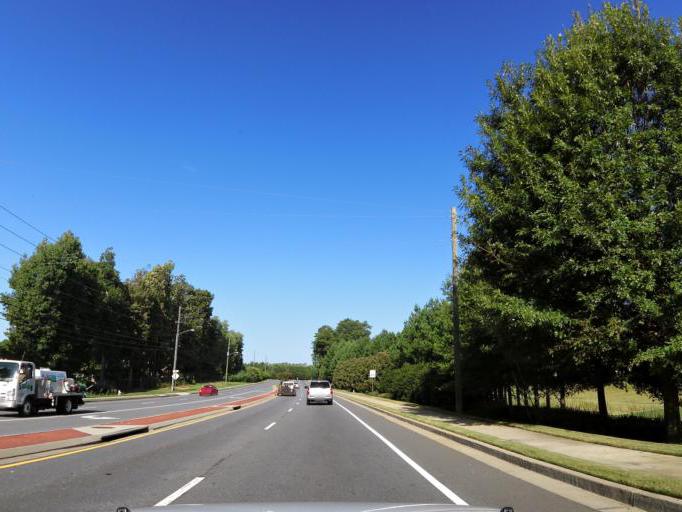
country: US
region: Georgia
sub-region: Cobb County
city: Kennesaw
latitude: 33.9857
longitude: -84.6174
